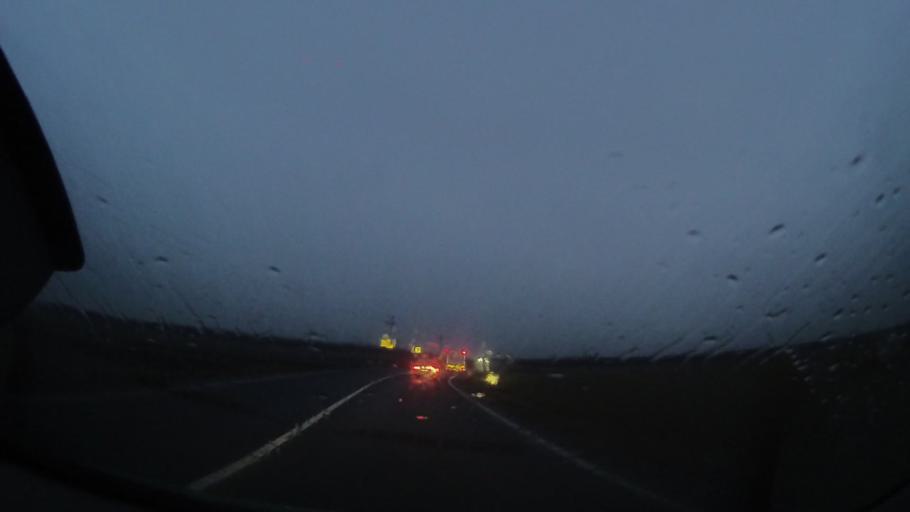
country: RO
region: Harghita
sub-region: Comuna Ditrau
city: Ditrau
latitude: 46.8198
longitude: 25.4919
